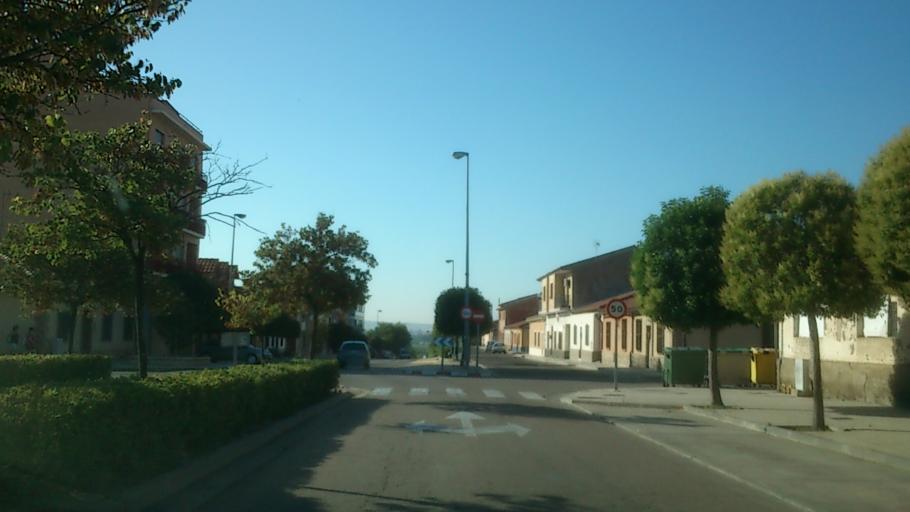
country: ES
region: Aragon
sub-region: Provincia de Zaragoza
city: Villanueva de Gallego
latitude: 41.7732
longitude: -0.8244
